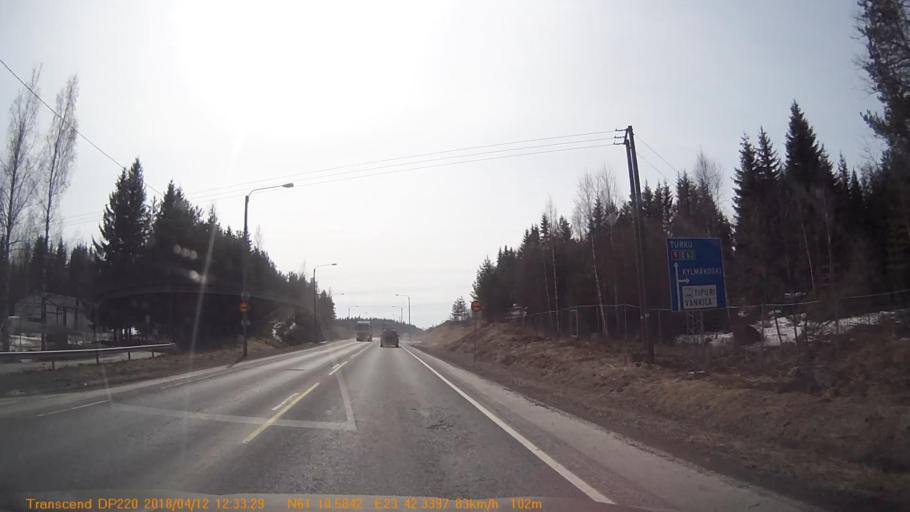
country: FI
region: Pirkanmaa
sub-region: Etelae-Pirkanmaa
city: Kylmaekoski
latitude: 61.1760
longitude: 23.7055
